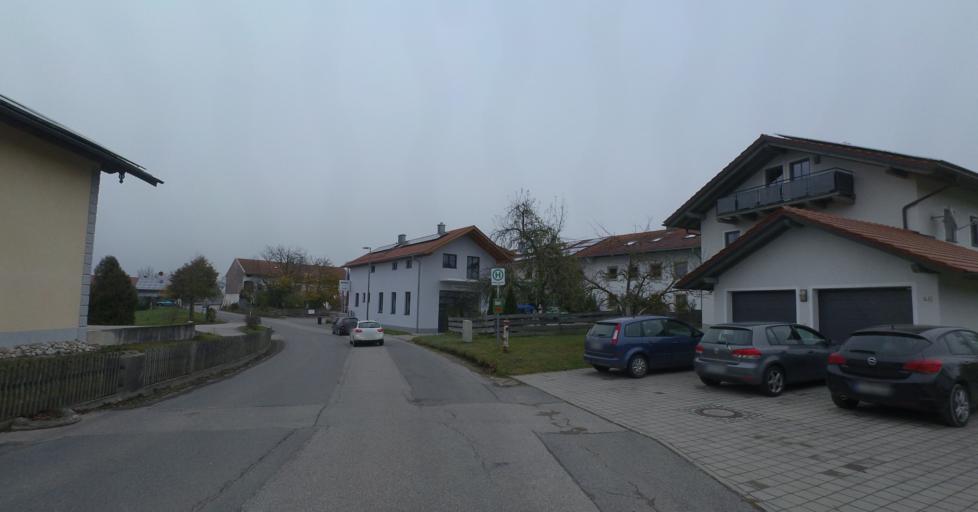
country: DE
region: Bavaria
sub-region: Upper Bavaria
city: Trostberg an der Alz
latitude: 47.9782
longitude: 12.5260
